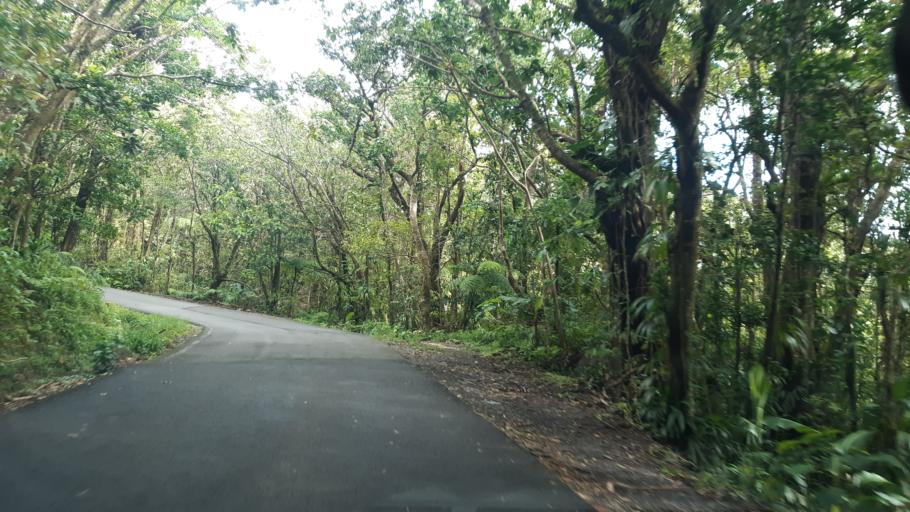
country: GP
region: Guadeloupe
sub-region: Guadeloupe
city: Saint-Claude
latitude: 16.0332
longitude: -61.6753
